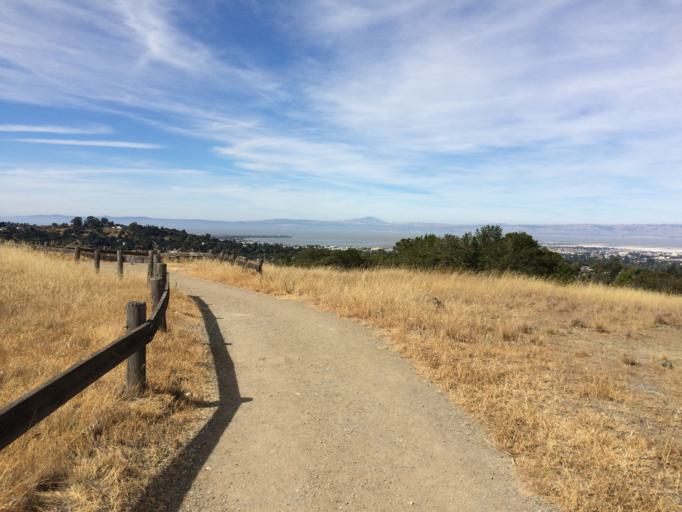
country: US
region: California
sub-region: San Mateo County
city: Emerald Lake Hills
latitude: 37.4636
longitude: -122.2787
